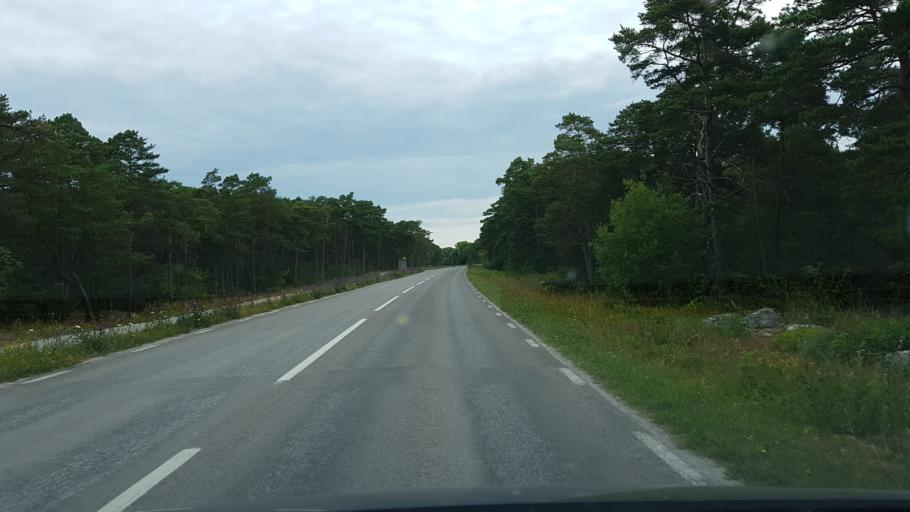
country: SE
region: Gotland
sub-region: Gotland
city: Visby
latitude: 57.7082
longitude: 18.3819
